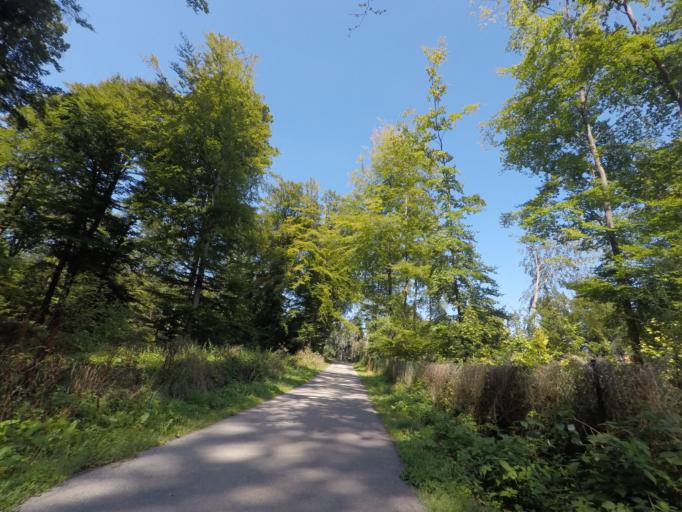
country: LU
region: Luxembourg
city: Bereldange
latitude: 49.6479
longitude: 6.1114
